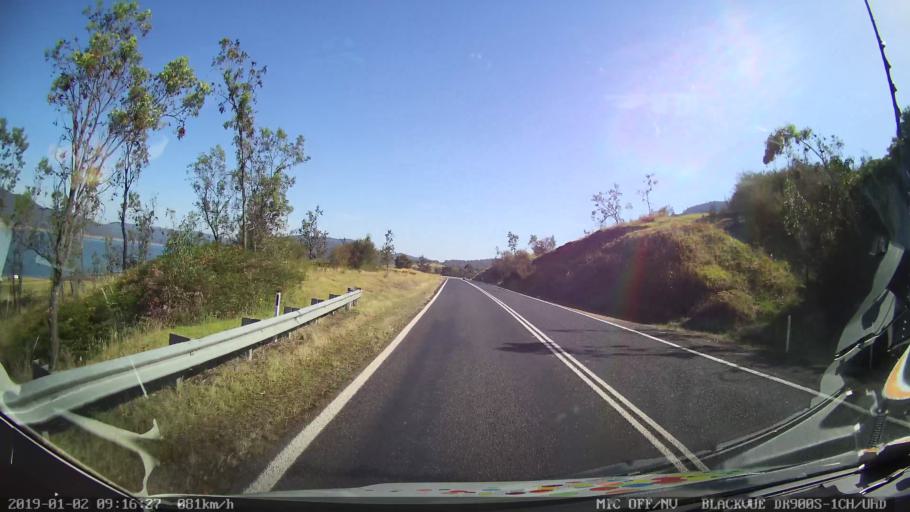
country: AU
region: New South Wales
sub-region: Tumut Shire
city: Tumut
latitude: -35.4532
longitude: 148.2841
